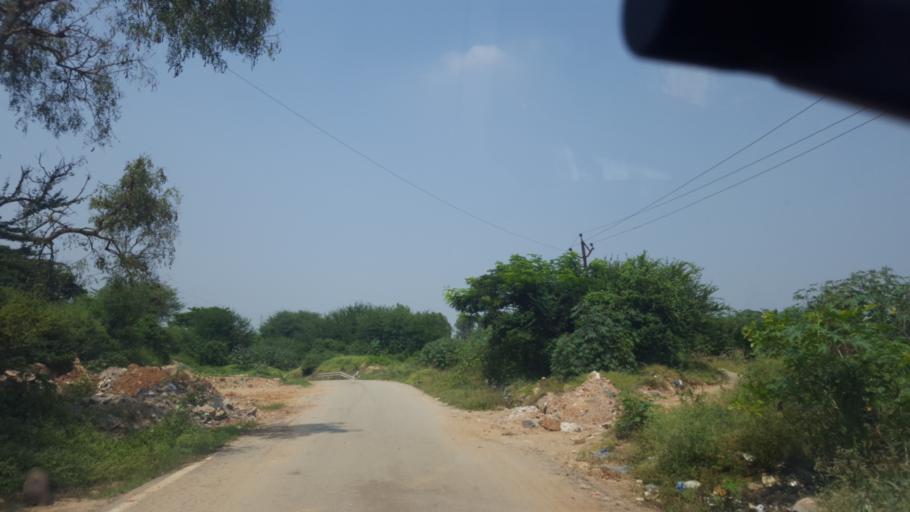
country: IN
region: Karnataka
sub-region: Bangalore Urban
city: Bangalore
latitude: 12.9391
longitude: 77.7074
